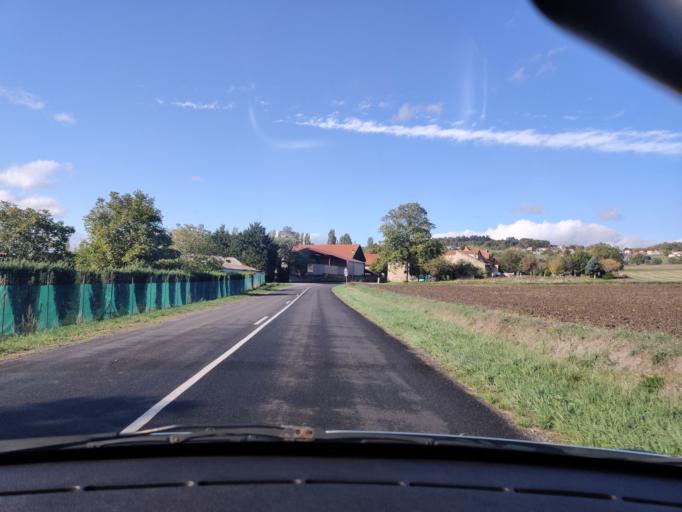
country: FR
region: Auvergne
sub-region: Departement du Puy-de-Dome
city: Aigueperse
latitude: 46.0079
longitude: 3.1738
